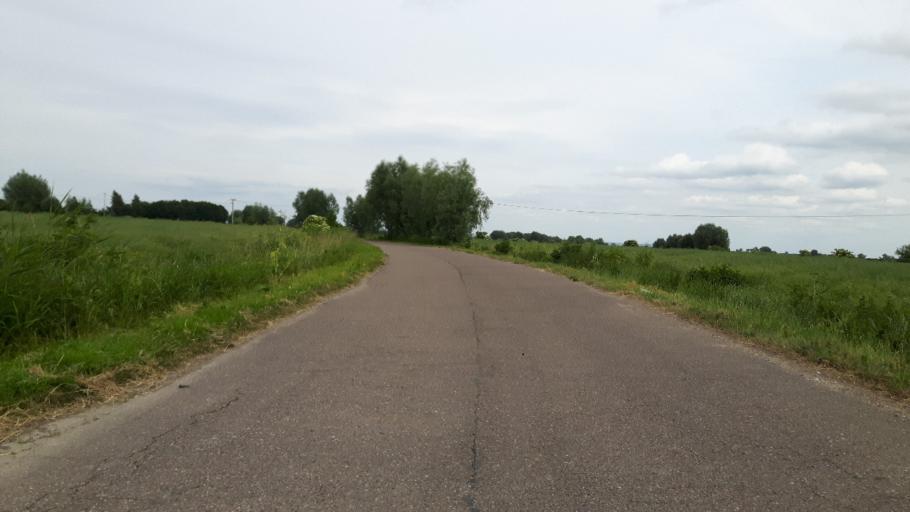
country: PL
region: Pomeranian Voivodeship
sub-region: Powiat nowodworski
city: Sztutowo
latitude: 54.2688
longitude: 19.1790
